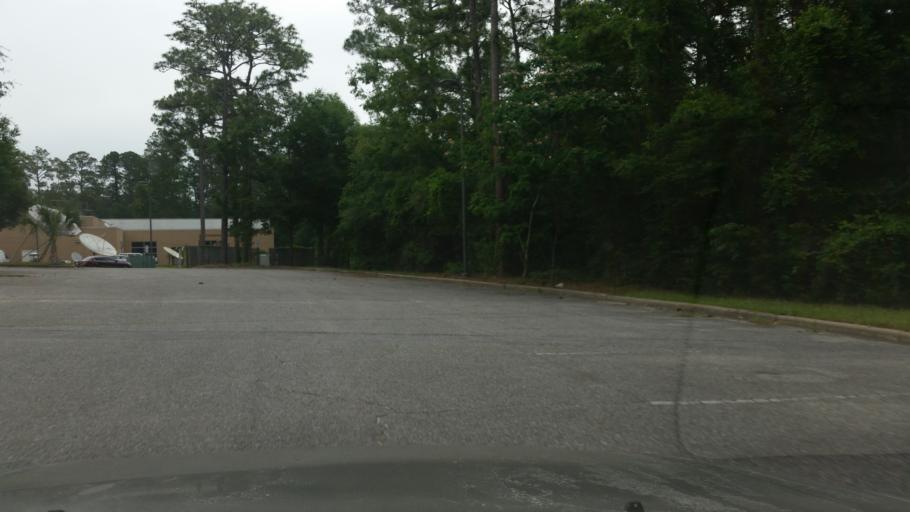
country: US
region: Florida
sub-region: Escambia County
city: Ferry Pass
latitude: 30.5432
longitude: -87.2206
